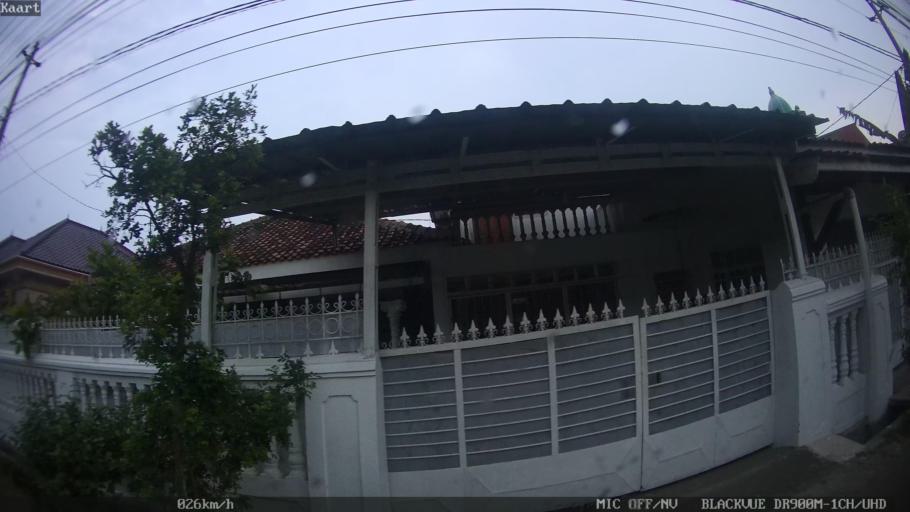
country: ID
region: Lampung
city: Kedaton
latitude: -5.3992
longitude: 105.2662
